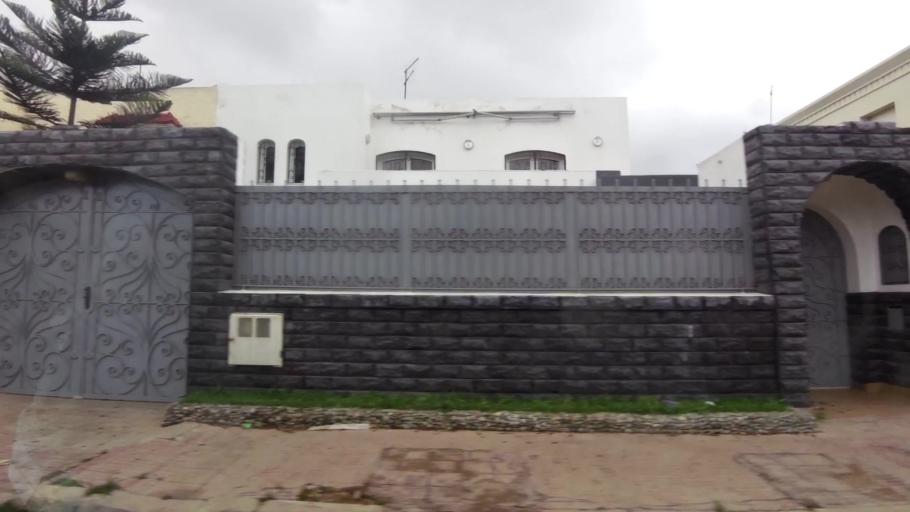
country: MA
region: Grand Casablanca
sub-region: Casablanca
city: Casablanca
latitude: 33.5831
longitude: -7.6807
